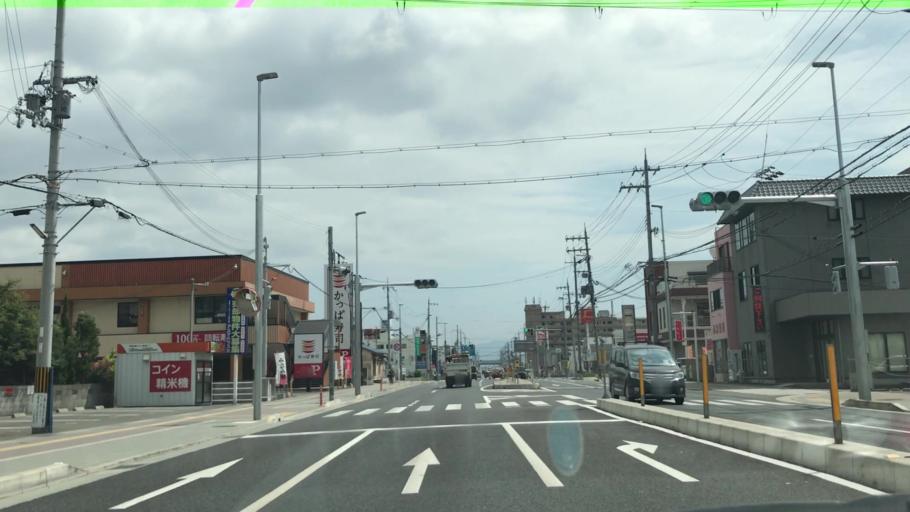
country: JP
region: Wakayama
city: Wakayama-shi
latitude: 34.2624
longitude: 135.1992
